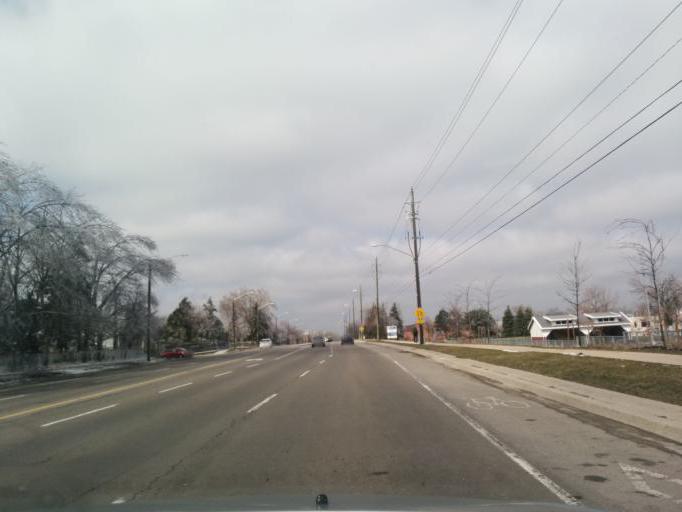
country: CA
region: Ontario
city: Waterloo
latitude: 43.4980
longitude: -80.5507
